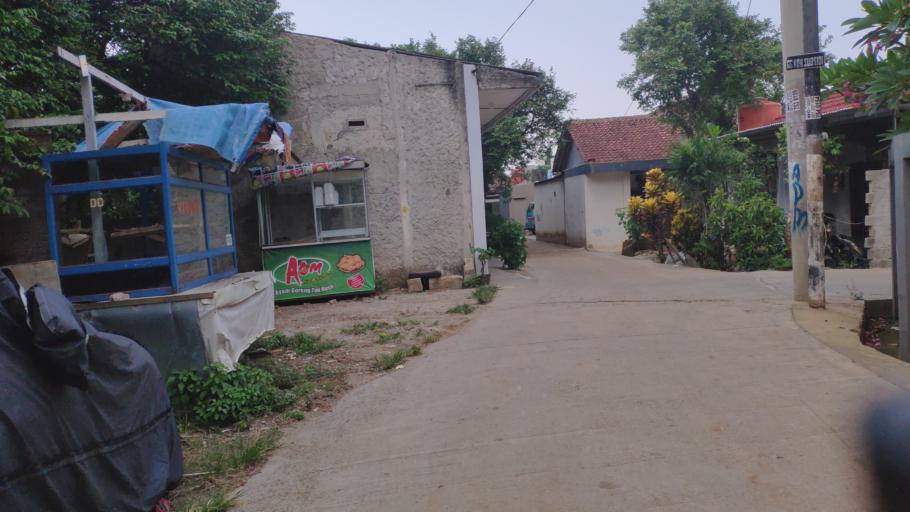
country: ID
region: West Java
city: Pamulang
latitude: -6.3557
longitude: 106.7725
